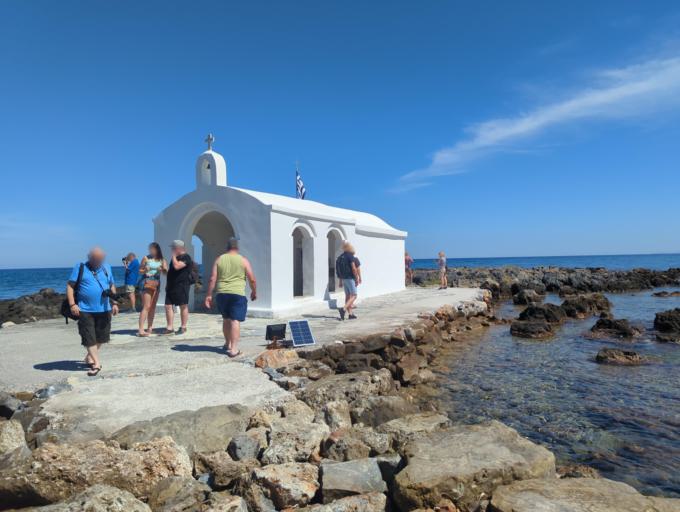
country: GR
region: Crete
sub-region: Nomos Chanias
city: Georgioupolis
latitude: 35.3656
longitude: 24.2637
